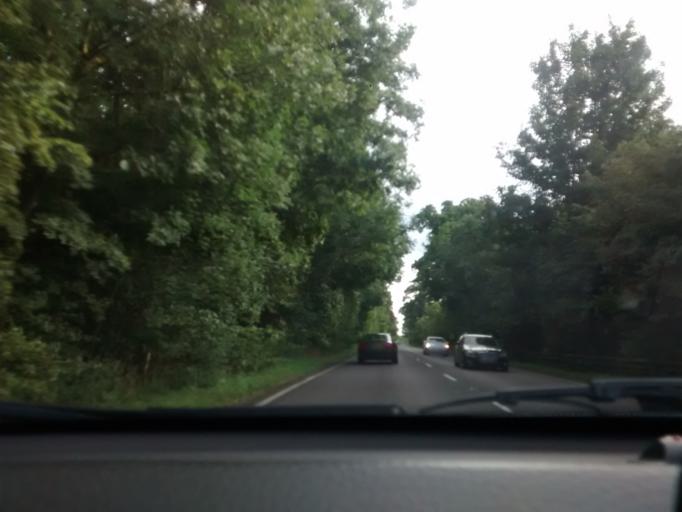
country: GB
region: England
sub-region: Norfolk
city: Downham Market
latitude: 52.5839
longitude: 0.3871
